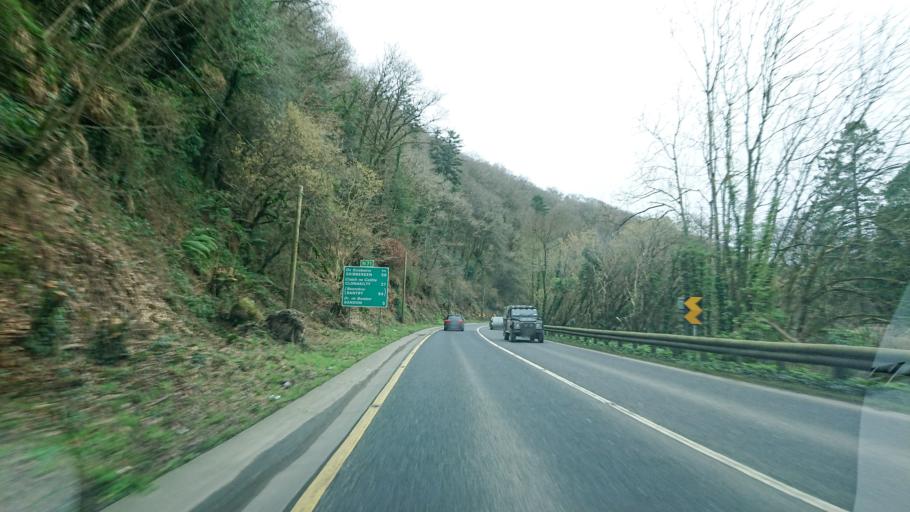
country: IE
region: Munster
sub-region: County Cork
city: Bandon
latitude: 51.7661
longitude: -8.6792
